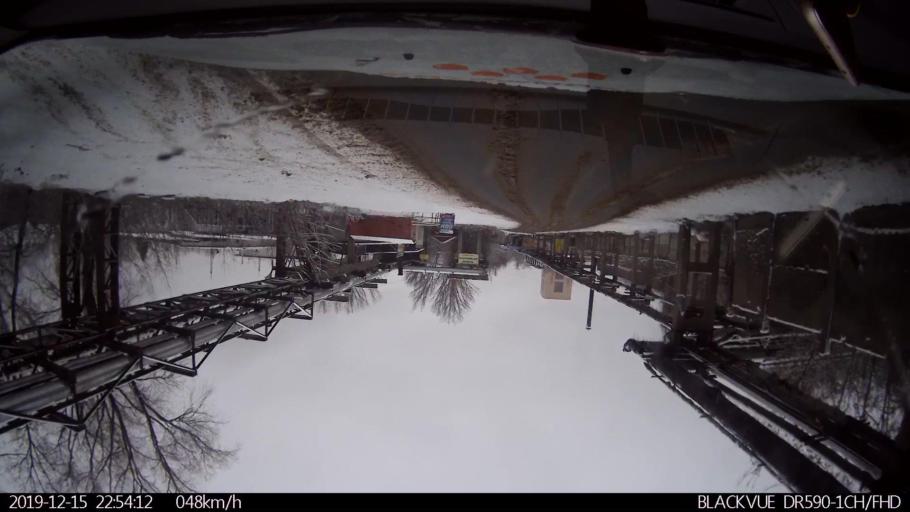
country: RU
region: Nizjnij Novgorod
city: Neklyudovo
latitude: 56.3544
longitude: 43.8804
